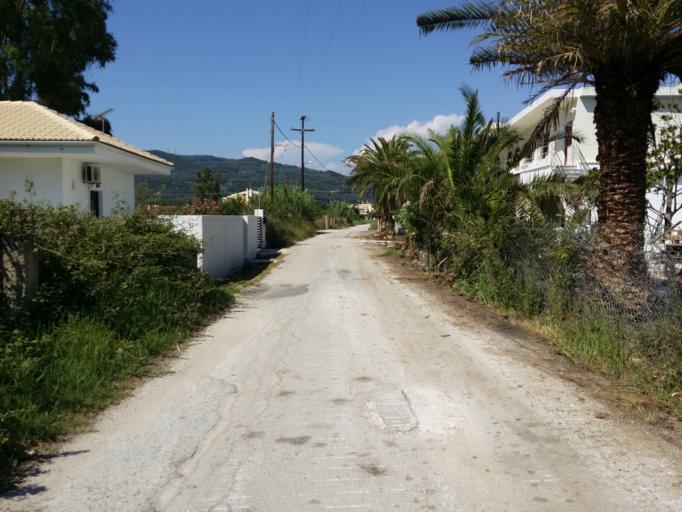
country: GR
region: Ionian Islands
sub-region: Nomos Kerkyras
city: Perivoli
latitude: 39.4291
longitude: 19.9433
